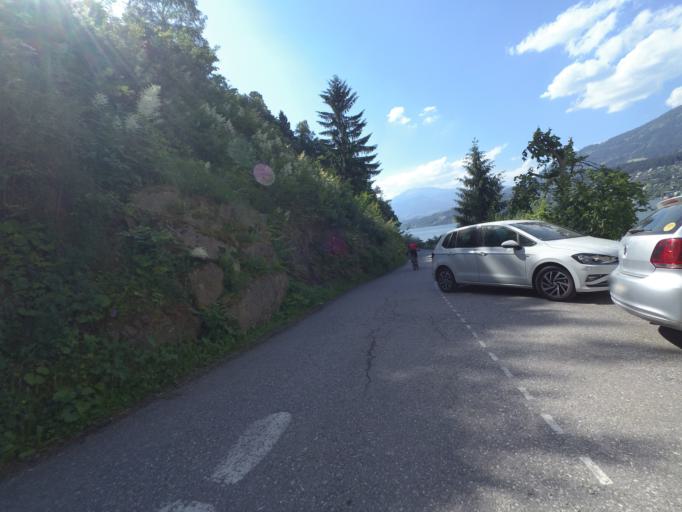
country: AT
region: Carinthia
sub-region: Politischer Bezirk Spittal an der Drau
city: Millstatt
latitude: 46.7932
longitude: 13.5692
